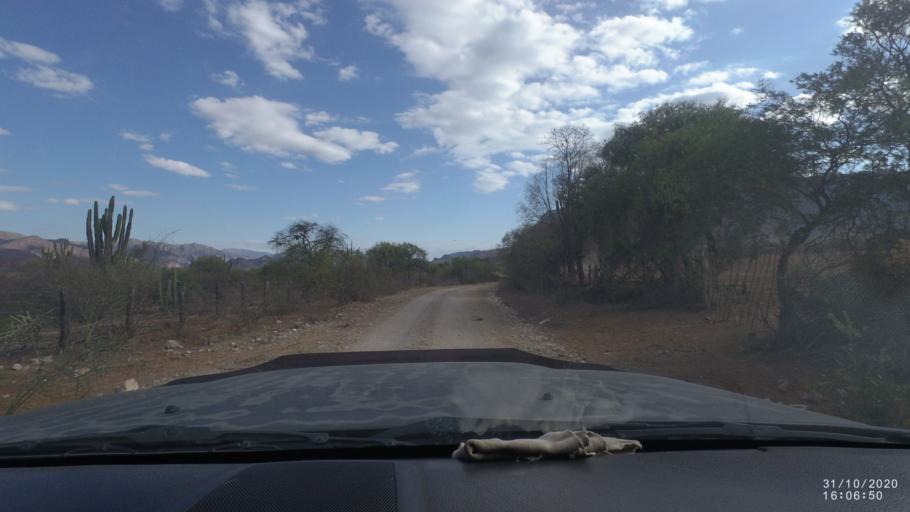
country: BO
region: Chuquisaca
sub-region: Provincia Zudanez
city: Mojocoya
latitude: -18.3758
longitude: -64.6455
